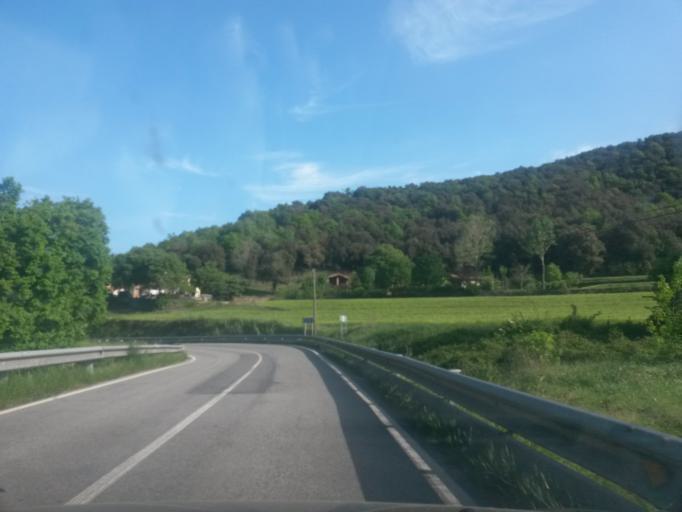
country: ES
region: Catalonia
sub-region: Provincia de Girona
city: Sant Feliu de Pallerols
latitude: 42.0741
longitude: 2.5153
